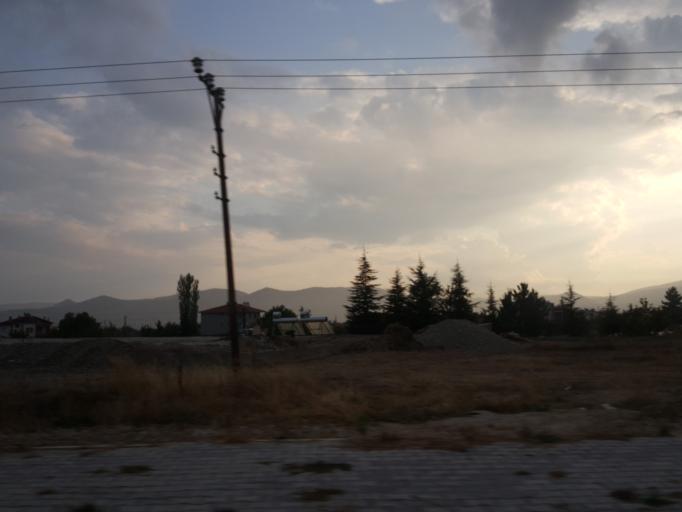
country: TR
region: Amasya
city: Gumushacikoy
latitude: 40.8789
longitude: 35.2266
